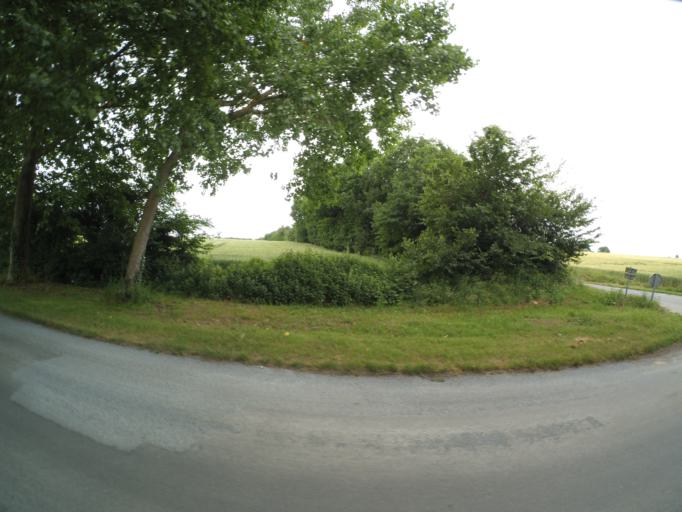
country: FR
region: Poitou-Charentes
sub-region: Departement de la Charente-Maritime
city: Saint-Laurent-de-la-Pree
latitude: 45.9870
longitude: -1.0126
